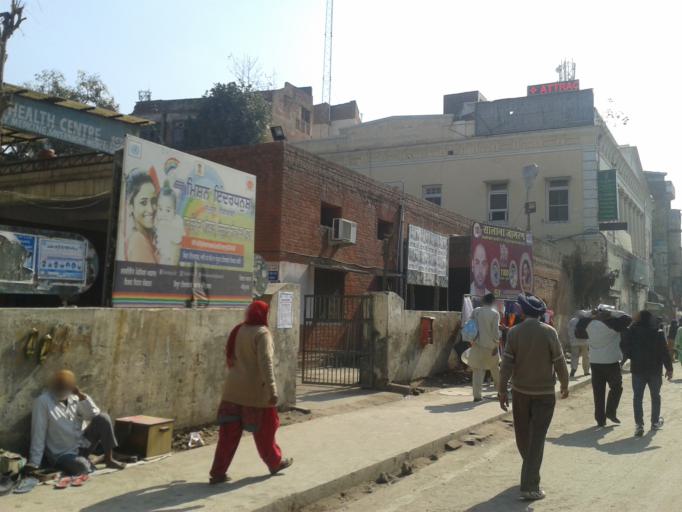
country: IN
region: Punjab
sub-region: Amritsar
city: Amritsar
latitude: 31.6233
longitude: 74.8795
